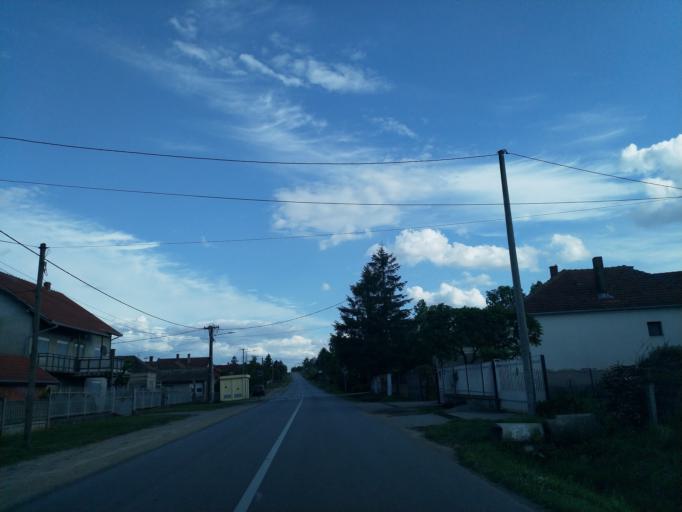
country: RS
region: Central Serbia
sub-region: Sumadijski Okrug
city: Lapovo
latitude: 44.1677
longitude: 21.0937
